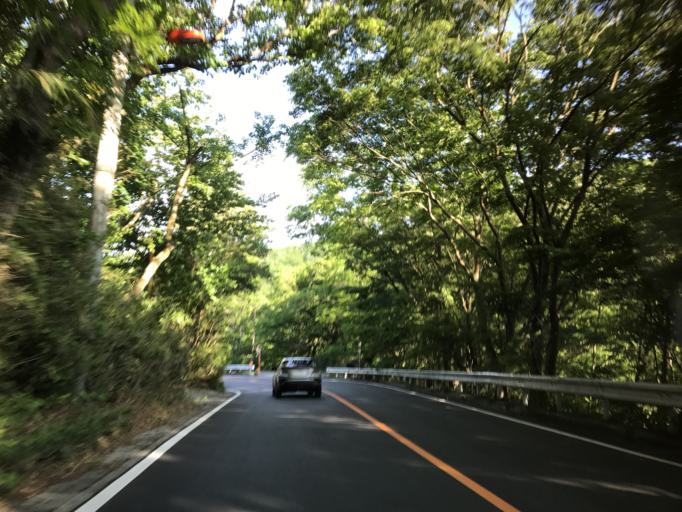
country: JP
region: Kanagawa
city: Hakone
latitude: 35.2594
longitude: 139.0336
